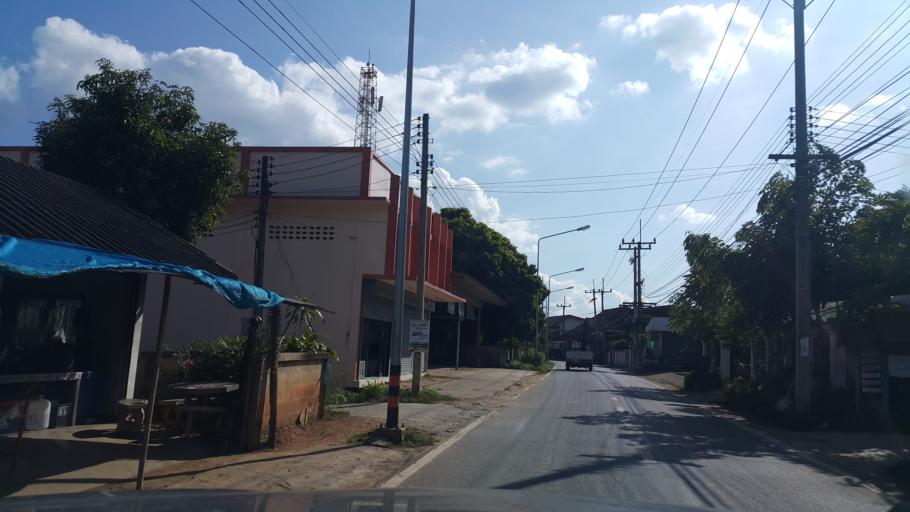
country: TH
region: Lamphun
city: Mae Tha
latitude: 18.5480
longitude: 99.2448
